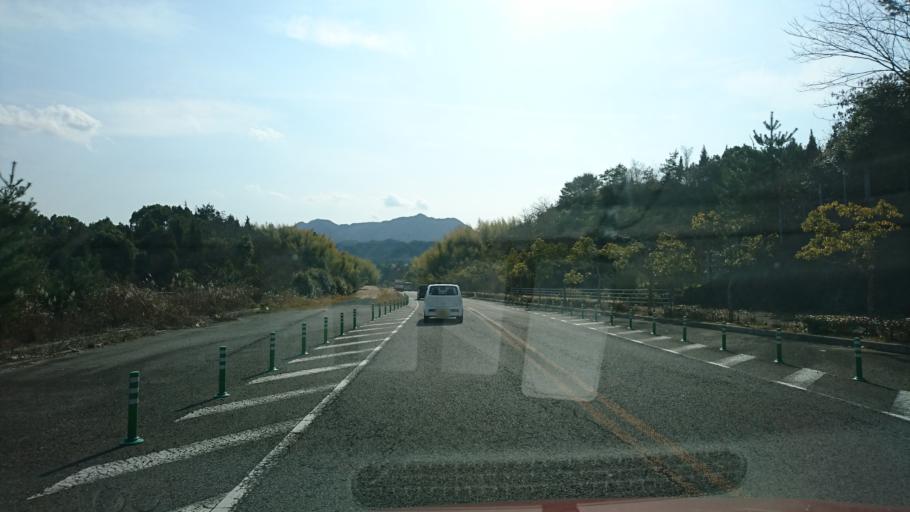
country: JP
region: Ehime
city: Saijo
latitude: 34.0102
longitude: 133.0339
